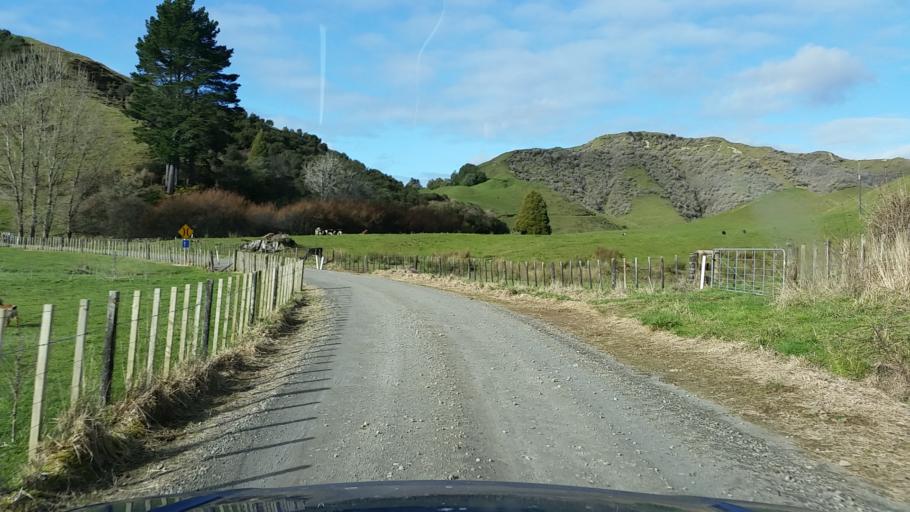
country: NZ
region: Taranaki
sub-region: South Taranaki District
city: Eltham
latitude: -39.2608
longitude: 174.5788
